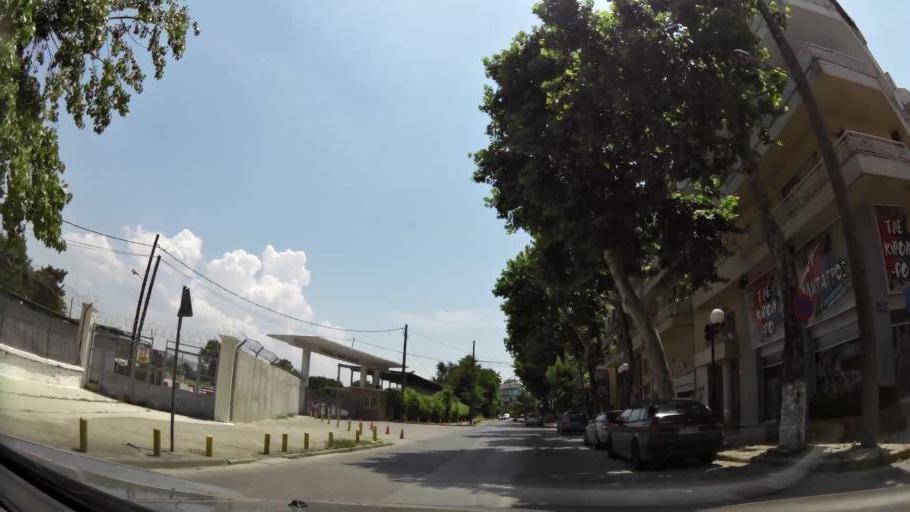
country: GR
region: Central Macedonia
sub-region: Nomos Thessalonikis
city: Evosmos
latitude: 40.6587
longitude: 22.9133
